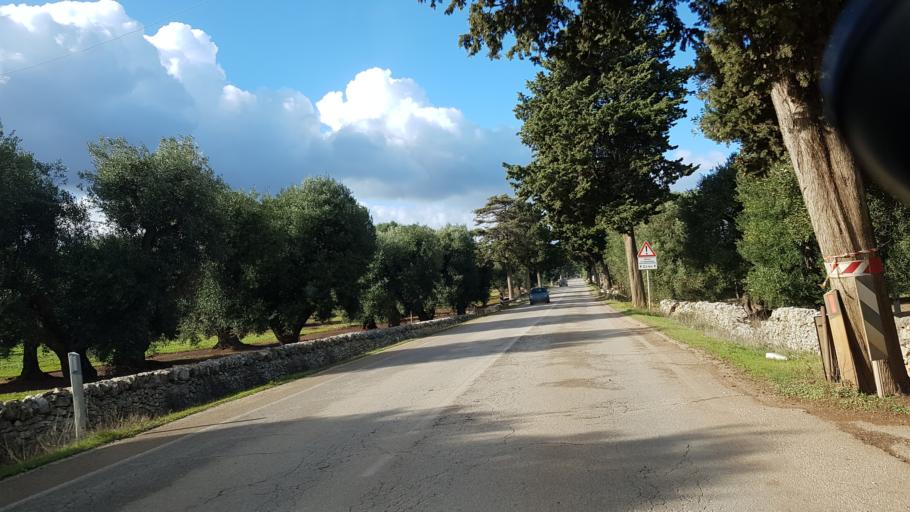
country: IT
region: Apulia
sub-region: Provincia di Brindisi
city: Montalbano
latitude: 40.7935
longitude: 17.4556
